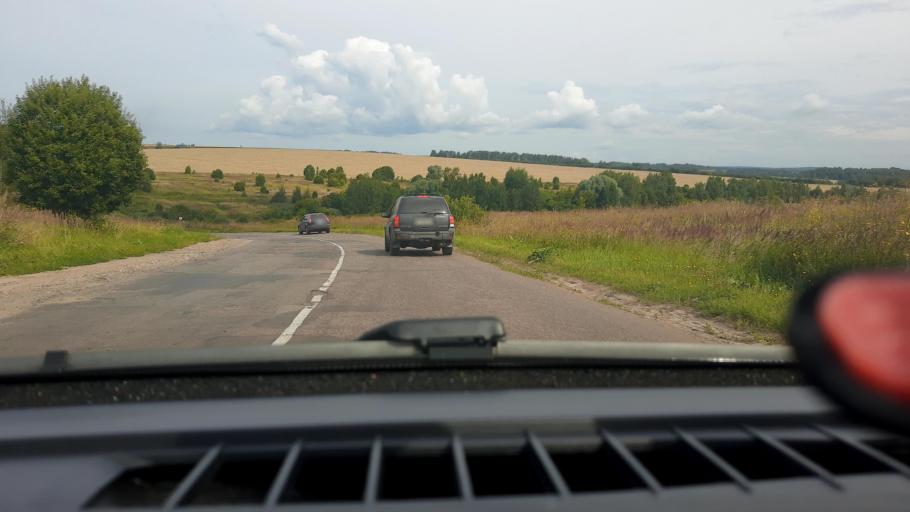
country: RU
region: Nizjnij Novgorod
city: Bogorodsk
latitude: 56.0786
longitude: 43.5755
